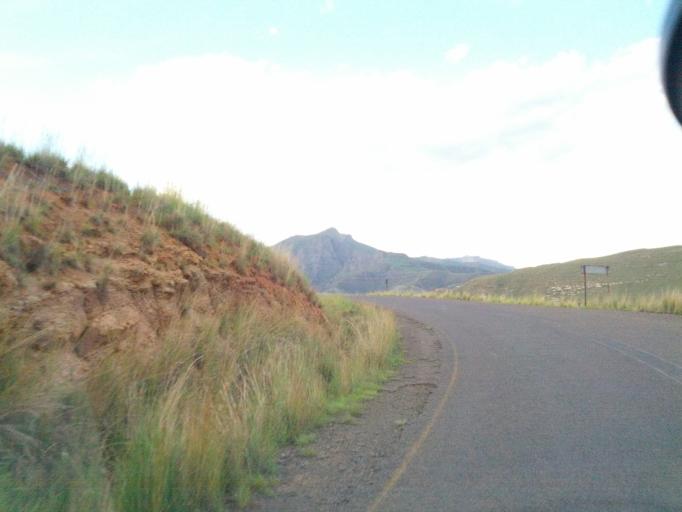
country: LS
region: Qacha's Nek
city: Qacha's Nek
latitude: -30.0756
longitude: 28.5795
